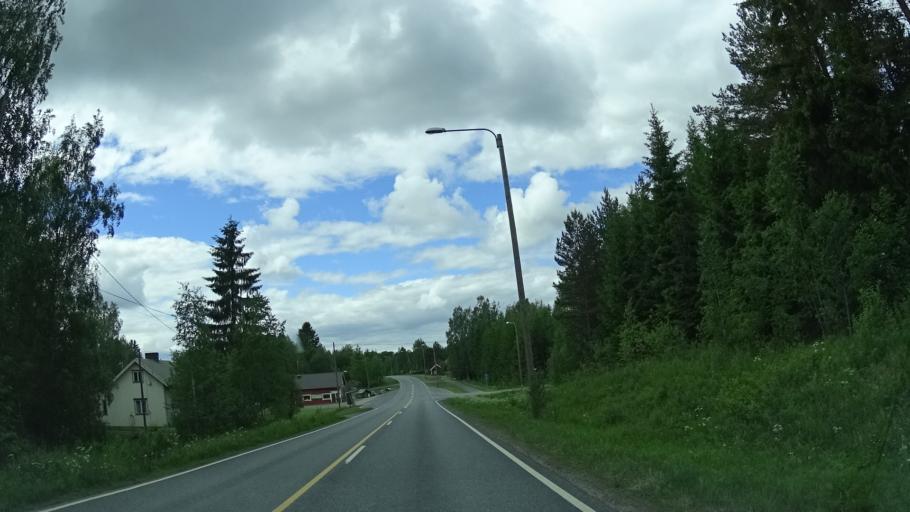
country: FI
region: Central Finland
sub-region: Joutsa
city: Luhanka
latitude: 61.8354
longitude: 25.8593
